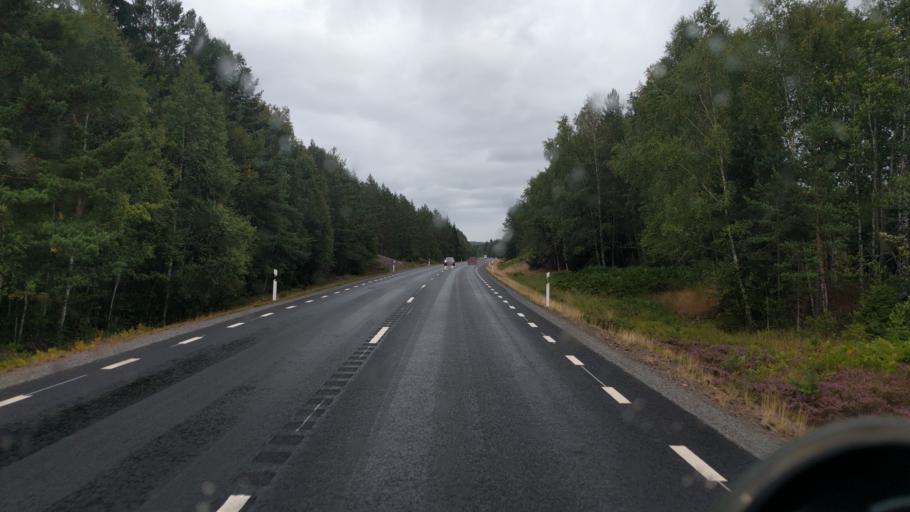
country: SE
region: Kalmar
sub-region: Vasterviks Kommun
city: Ankarsrum
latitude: 57.7222
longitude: 16.3648
